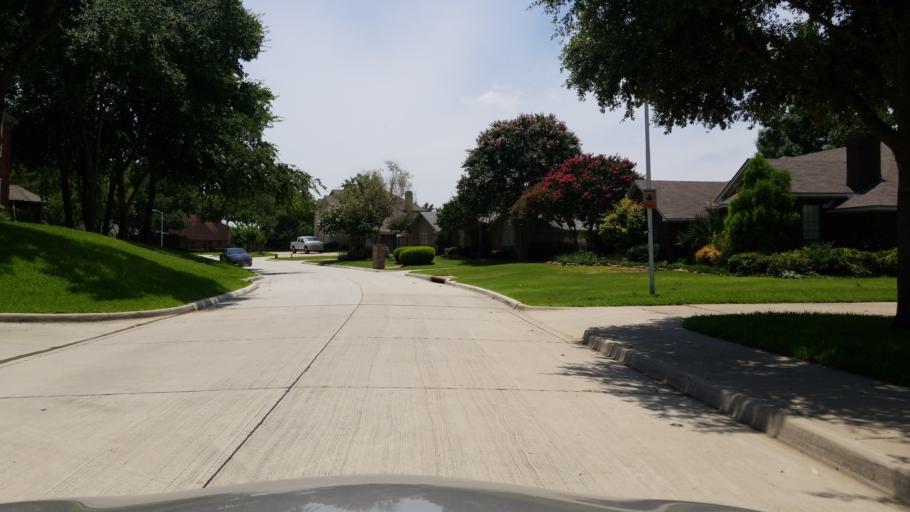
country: US
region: Texas
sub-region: Dallas County
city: Grand Prairie
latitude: 32.6842
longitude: -96.9887
